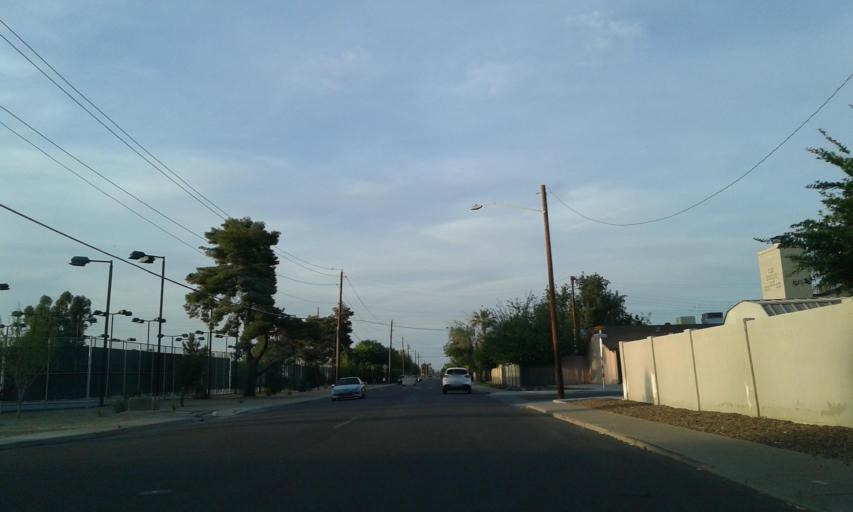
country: US
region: Arizona
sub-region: Maricopa County
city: Glendale
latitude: 33.5295
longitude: -112.1039
